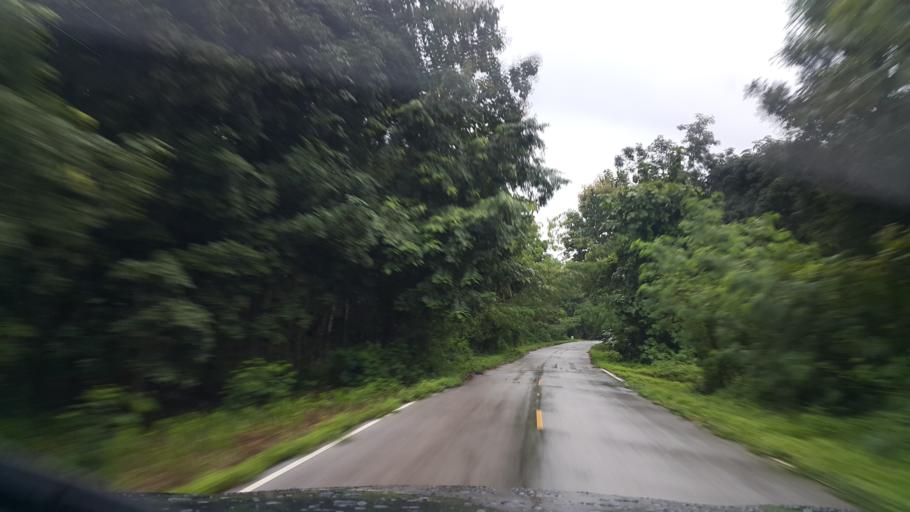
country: TH
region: Phayao
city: Phu Sang
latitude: 19.6130
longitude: 100.4076
